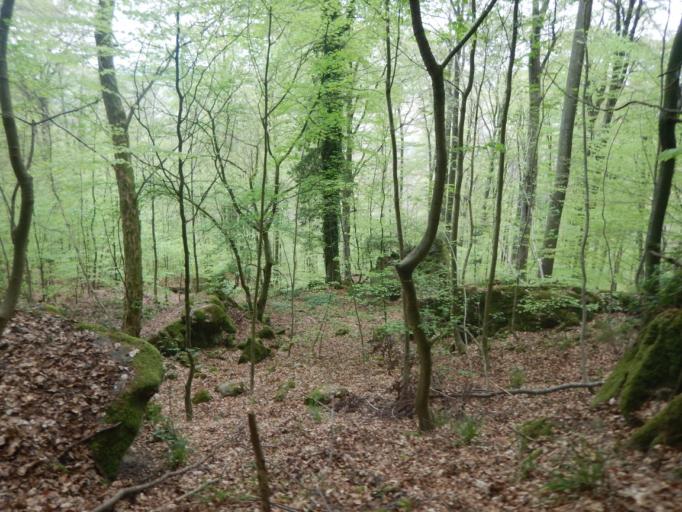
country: LU
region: Grevenmacher
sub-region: Canton d'Echternach
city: Berdorf
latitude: 49.8065
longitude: 6.3270
